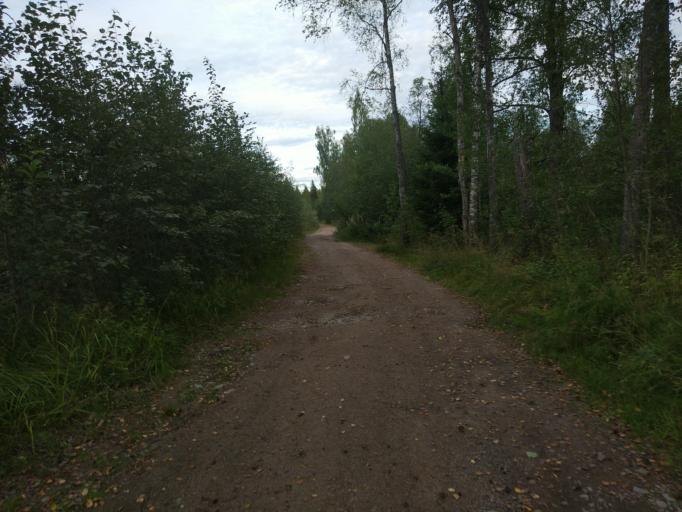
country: RU
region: Leningrad
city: Kuznechnoye
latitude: 61.1184
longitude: 29.5993
